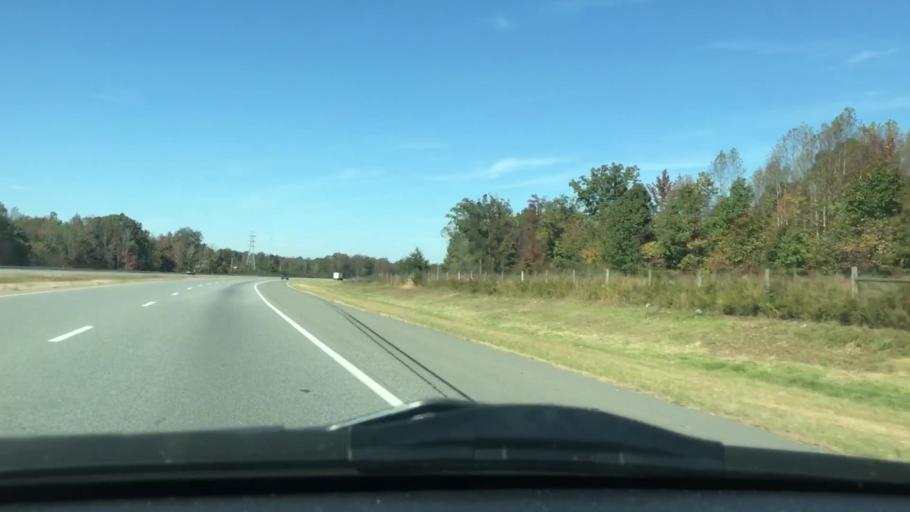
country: US
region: North Carolina
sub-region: Randolph County
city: Archdale
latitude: 35.8813
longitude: -79.9109
